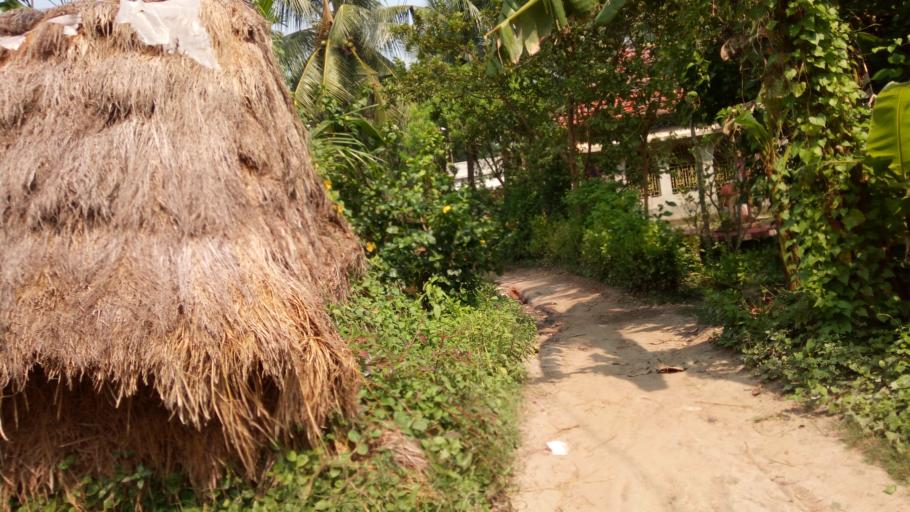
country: IN
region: West Bengal
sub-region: Purba Medinipur
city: Mahishadal
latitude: 22.1717
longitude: 87.9145
